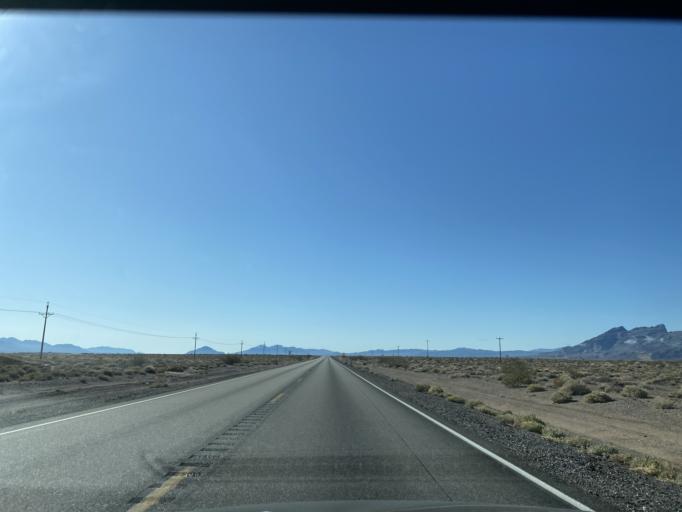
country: US
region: Nevada
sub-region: Nye County
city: Pahrump
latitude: 36.4535
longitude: -116.4218
